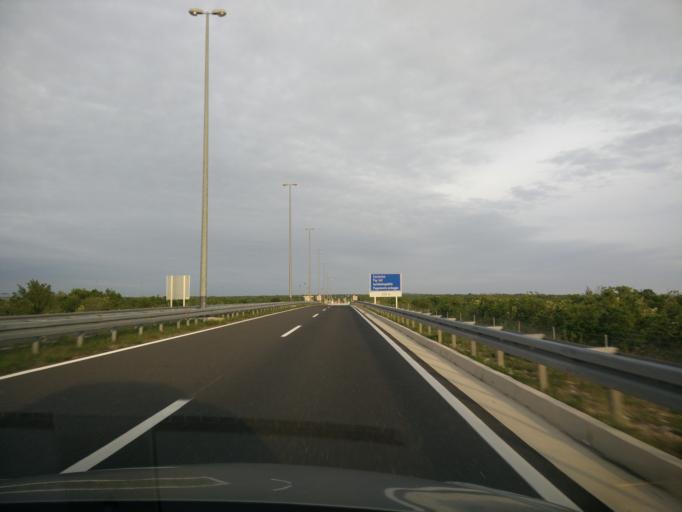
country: HR
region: Zadarska
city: Galovac
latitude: 44.1174
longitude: 15.4314
